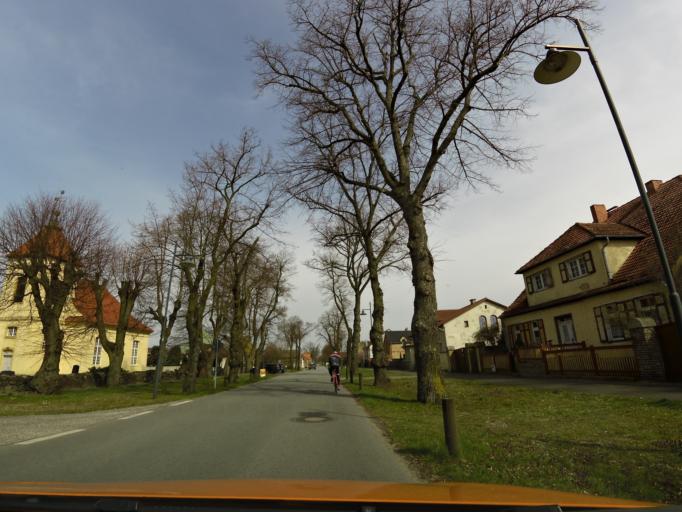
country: DE
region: Brandenburg
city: Stahnsdorf
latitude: 52.3273
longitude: 13.1619
